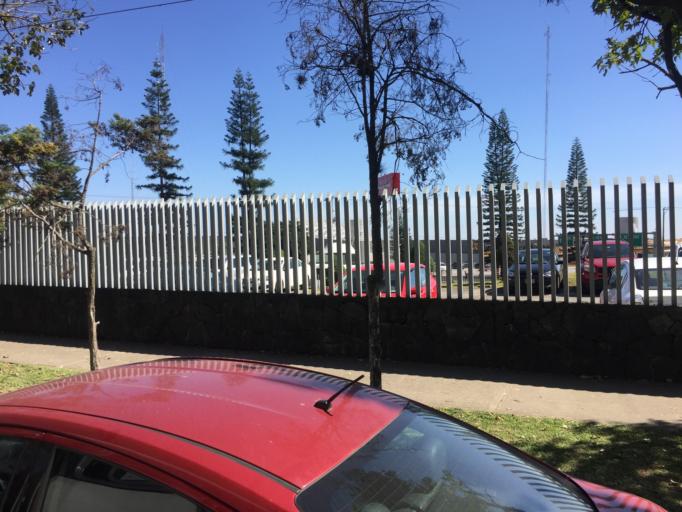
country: MX
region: Veracruz
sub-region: Xalapa
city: Xalapa de Enriquez
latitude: 19.5395
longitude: -96.9086
